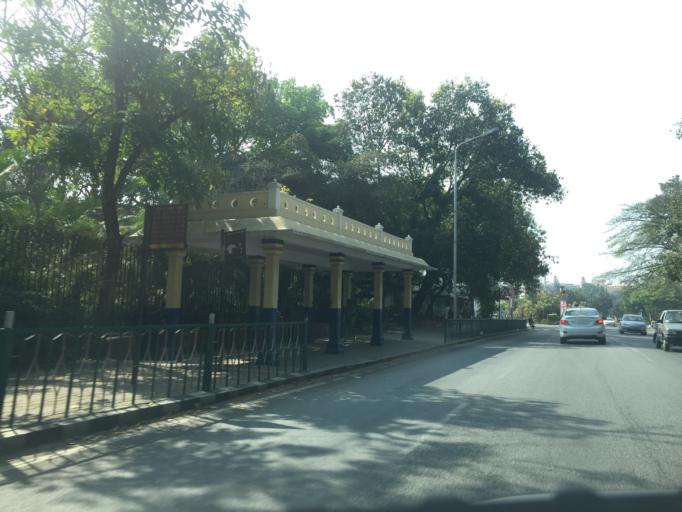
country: IN
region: Karnataka
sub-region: Bangalore Urban
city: Bangalore
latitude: 12.9825
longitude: 77.5886
